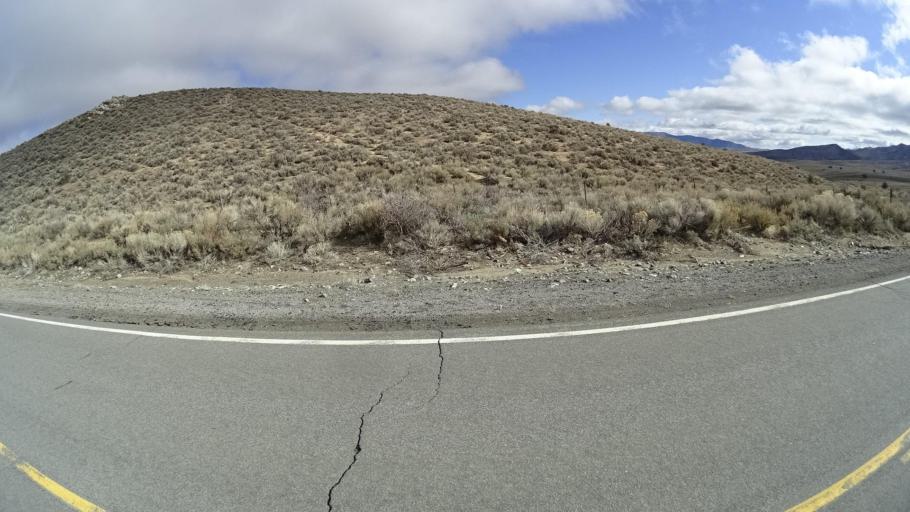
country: US
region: Nevada
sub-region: Washoe County
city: Cold Springs
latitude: 39.8006
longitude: -119.9046
